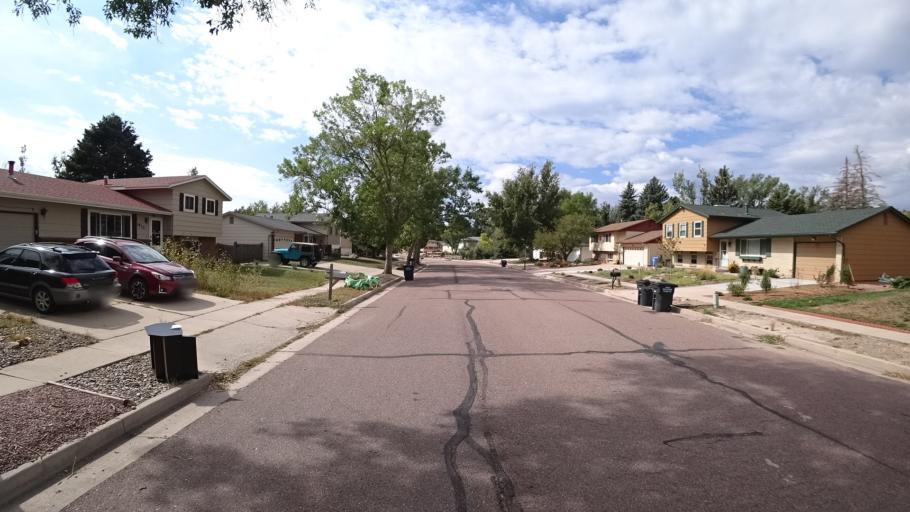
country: US
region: Colorado
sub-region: El Paso County
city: Cimarron Hills
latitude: 38.8595
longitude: -104.7324
